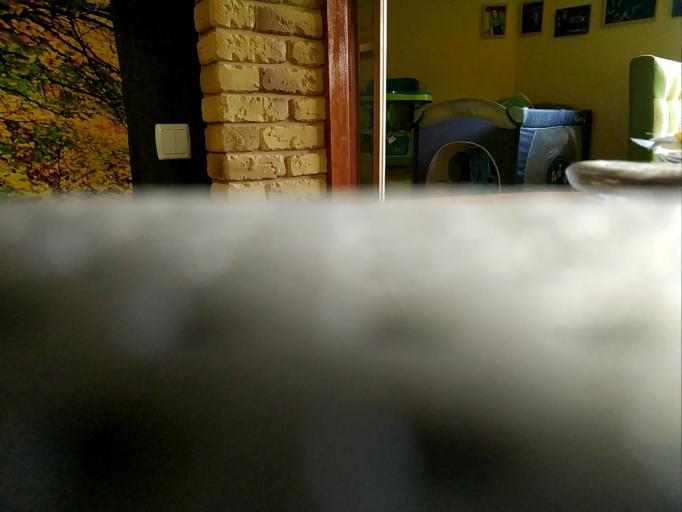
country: RU
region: Kaluga
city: Seredeyskiy
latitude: 53.9040
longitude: 35.3539
